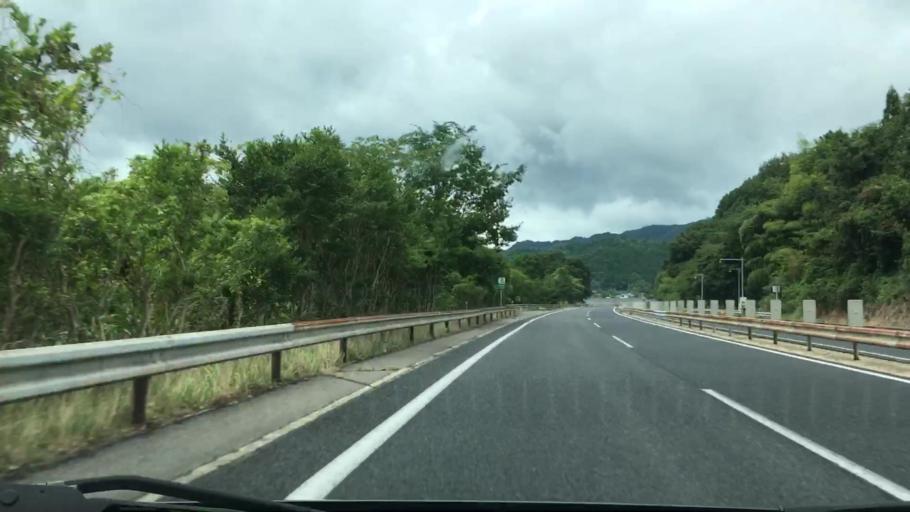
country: JP
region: Okayama
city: Takahashi
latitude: 34.9870
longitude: 133.7043
